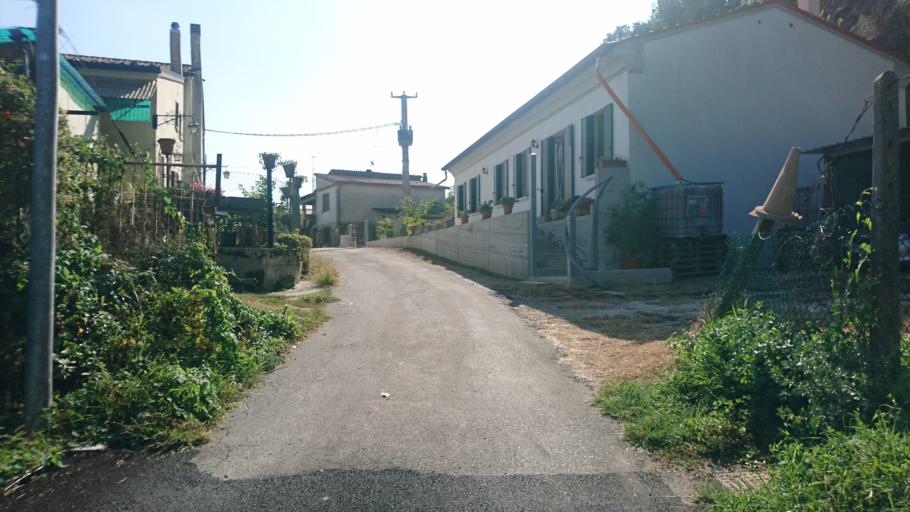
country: IT
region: Veneto
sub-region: Provincia di Padova
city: Battaglia Terme
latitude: 45.2774
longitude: 11.7585
